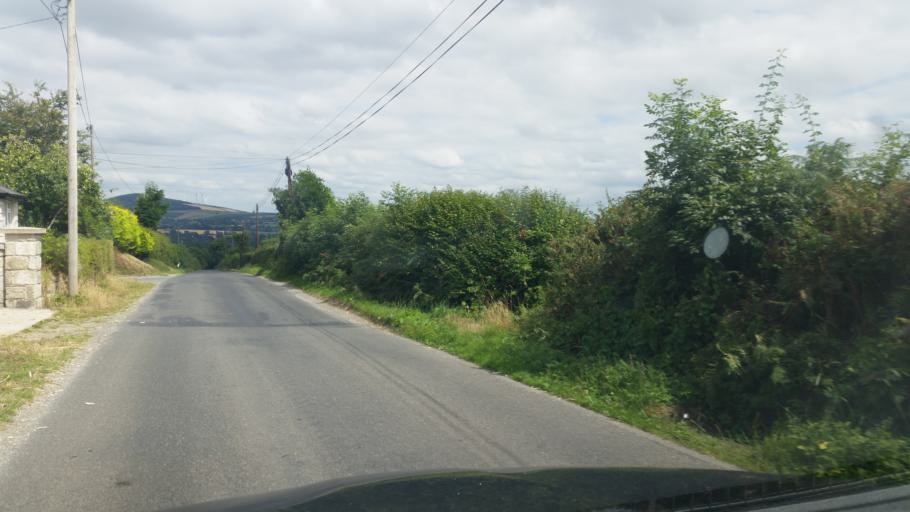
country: IE
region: Leinster
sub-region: Loch Garman
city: Bunclody
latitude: 52.6498
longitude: -6.6822
